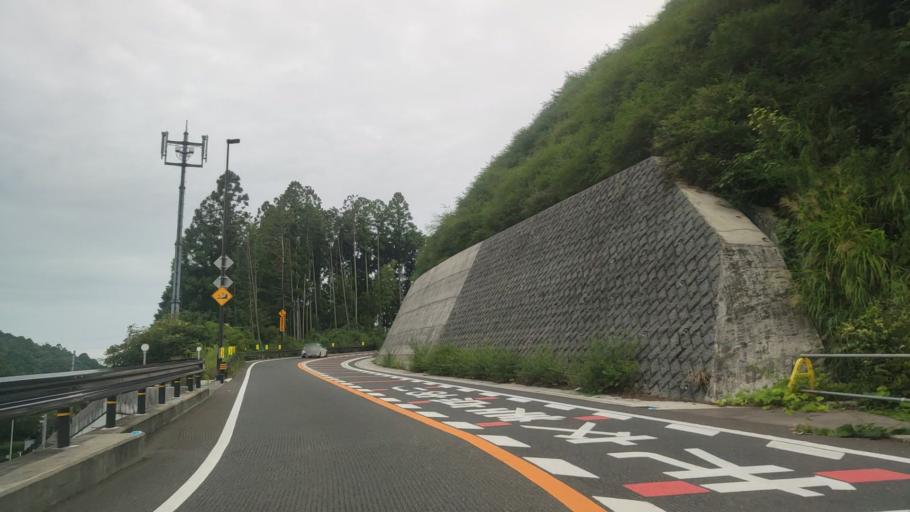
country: JP
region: Wakayama
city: Hashimoto
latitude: 34.3944
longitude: 135.5959
